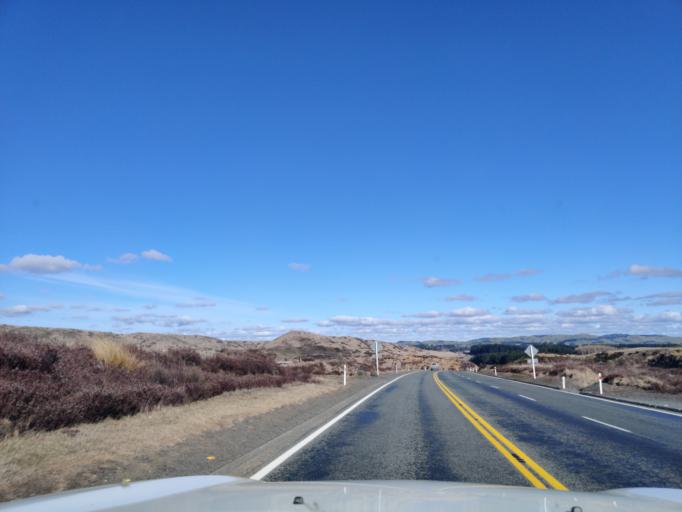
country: NZ
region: Manawatu-Wanganui
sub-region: Ruapehu District
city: Waiouru
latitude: -39.4319
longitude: 175.6850
